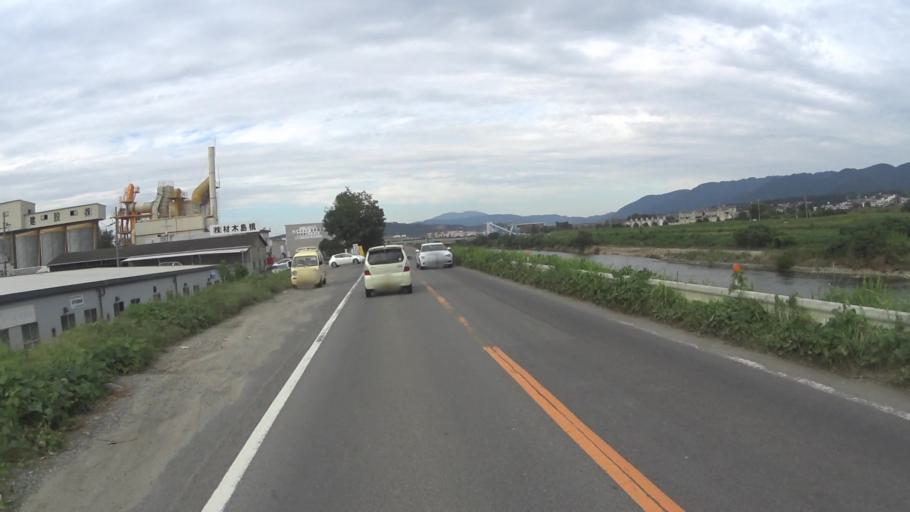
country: JP
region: Kyoto
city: Uji
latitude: 34.9105
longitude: 135.7891
